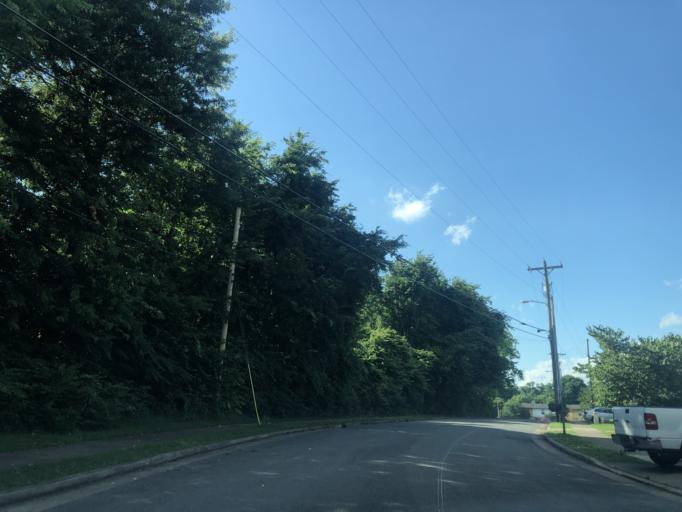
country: US
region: Tennessee
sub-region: Davidson County
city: Nashville
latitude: 36.1776
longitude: -86.7701
